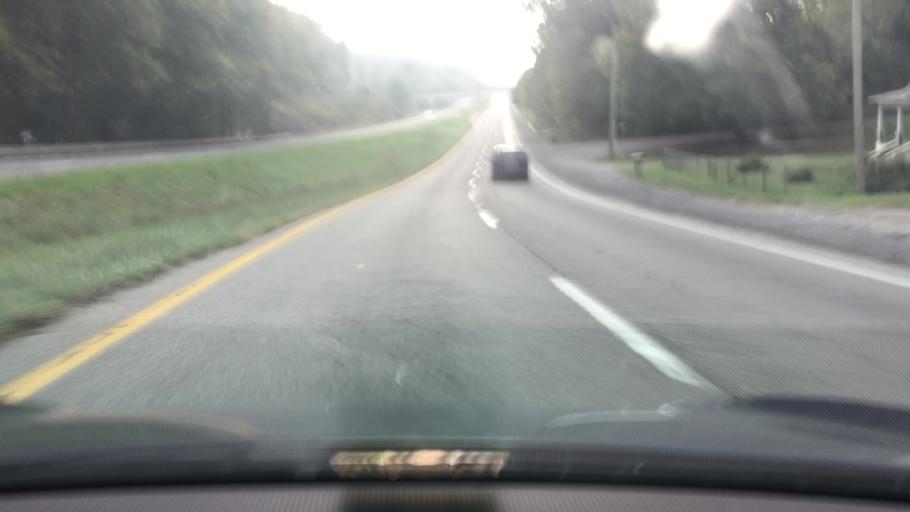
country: US
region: Virginia
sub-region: Botetourt County
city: Blue Ridge
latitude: 37.3968
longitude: -79.7506
